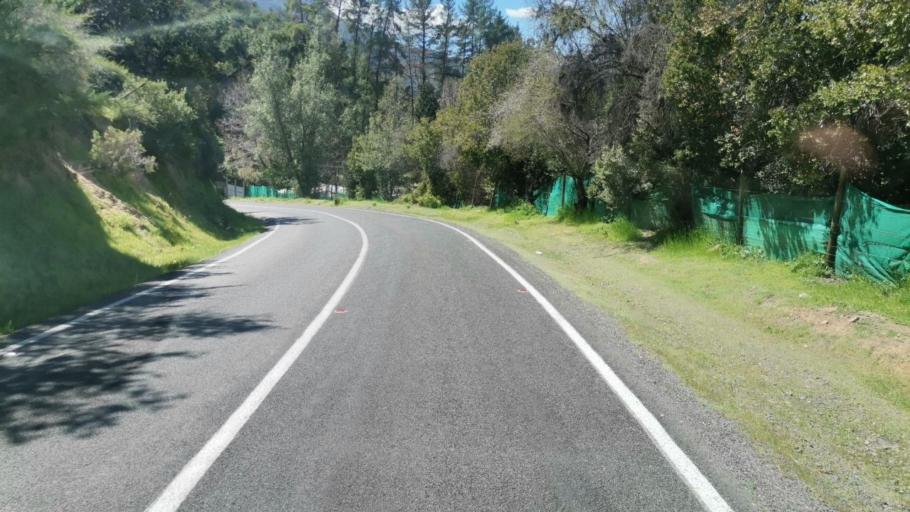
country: CL
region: Valparaiso
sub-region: Provincia de Marga Marga
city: Limache
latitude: -33.1794
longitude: -71.1738
